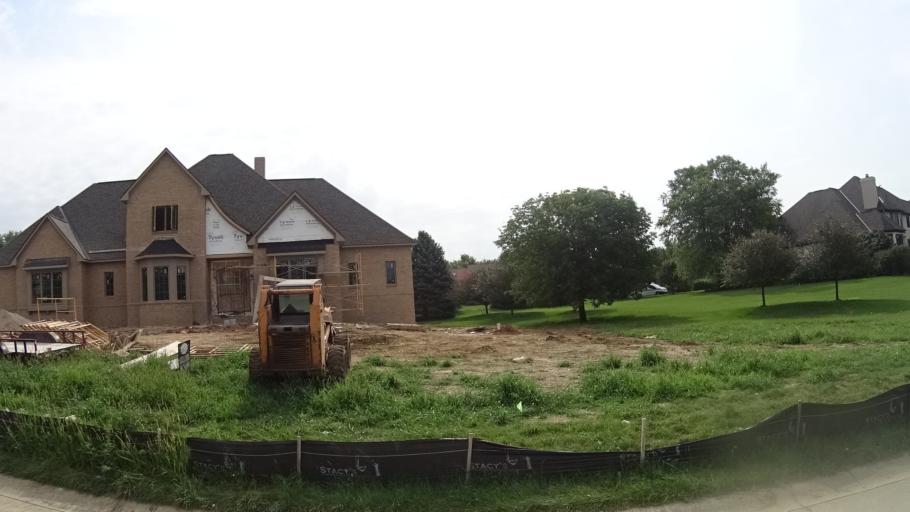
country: US
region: Indiana
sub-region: Madison County
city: Pendleton
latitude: 40.0129
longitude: -85.7887
